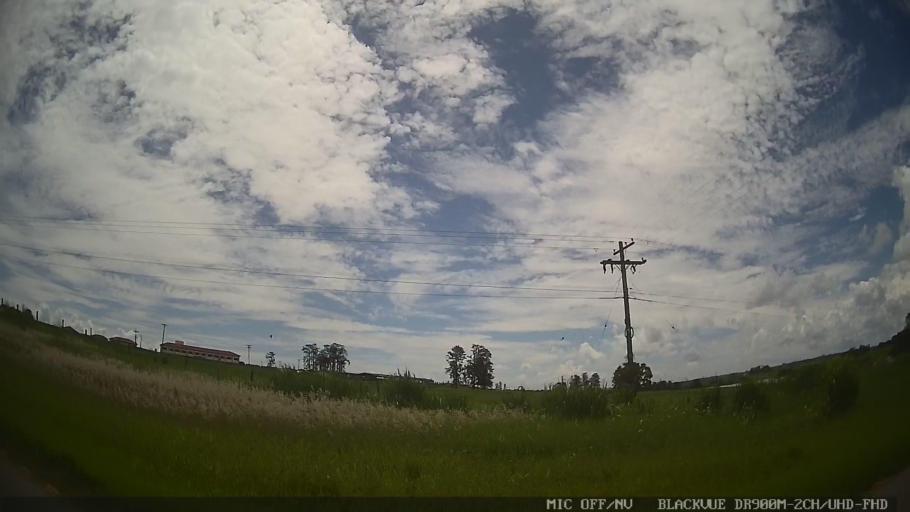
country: BR
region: Sao Paulo
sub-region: Conchas
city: Conchas
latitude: -23.0591
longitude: -47.9653
